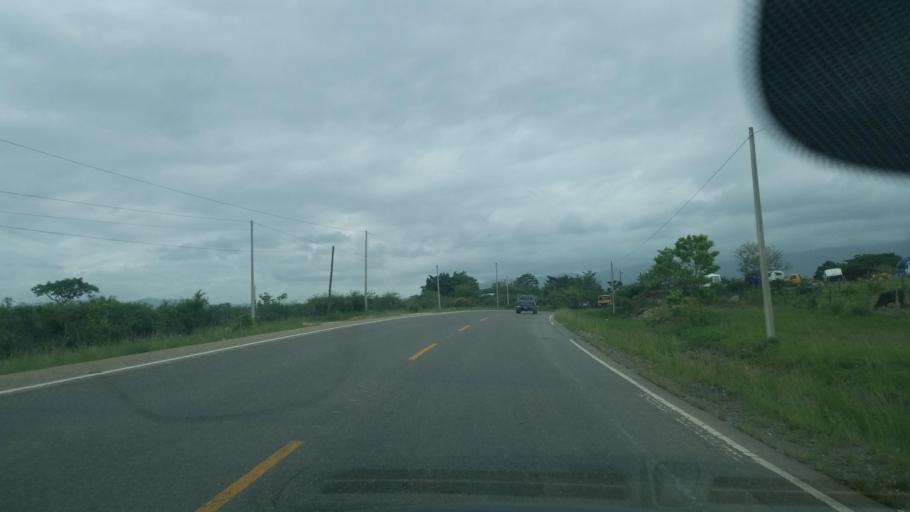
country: HN
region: Ocotepeque
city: Sensenti
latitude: 14.5141
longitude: -88.9521
